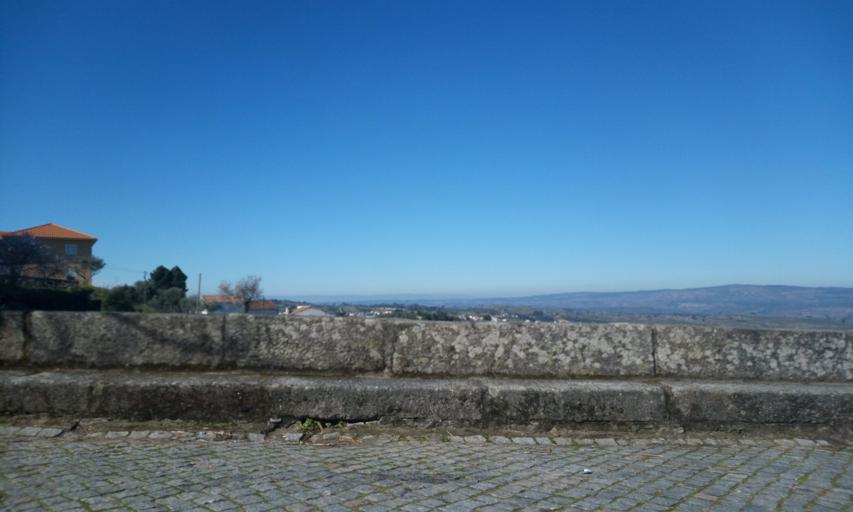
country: PT
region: Guarda
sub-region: Fornos de Algodres
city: Fornos de Algodres
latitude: 40.5189
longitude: -7.5549
